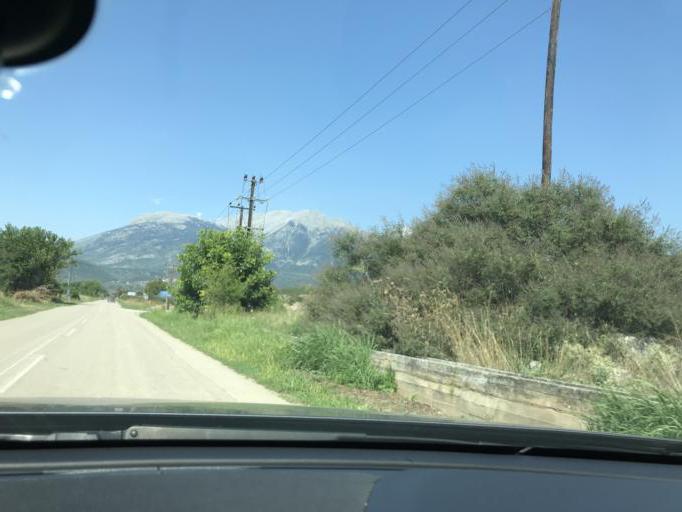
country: GR
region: Central Greece
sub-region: Nomos Fthiotidos
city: Elateia
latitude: 38.5250
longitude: 22.7907
